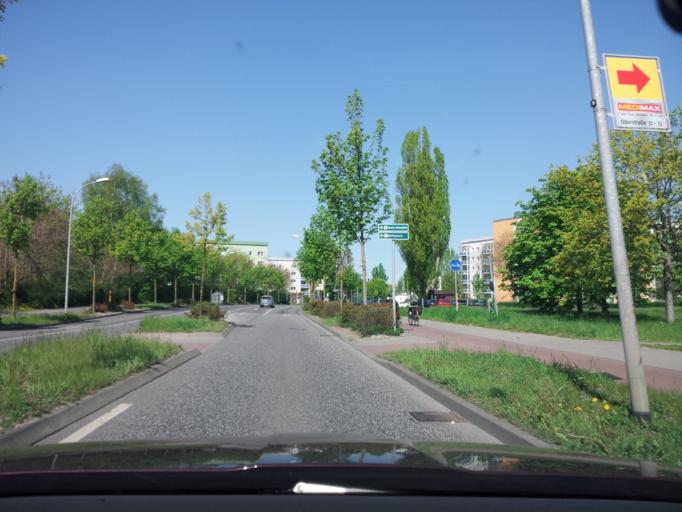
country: DE
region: Brandenburg
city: Teltow
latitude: 52.3982
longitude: 13.2734
